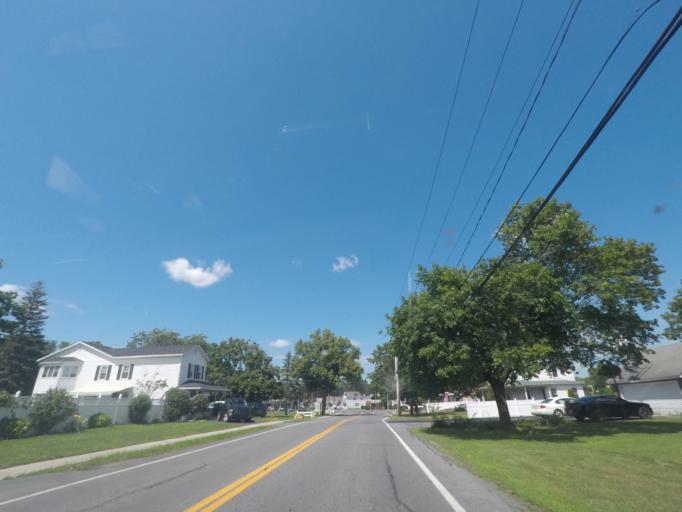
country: US
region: New York
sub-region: Schenectady County
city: Rotterdam
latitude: 42.7795
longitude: -73.9578
